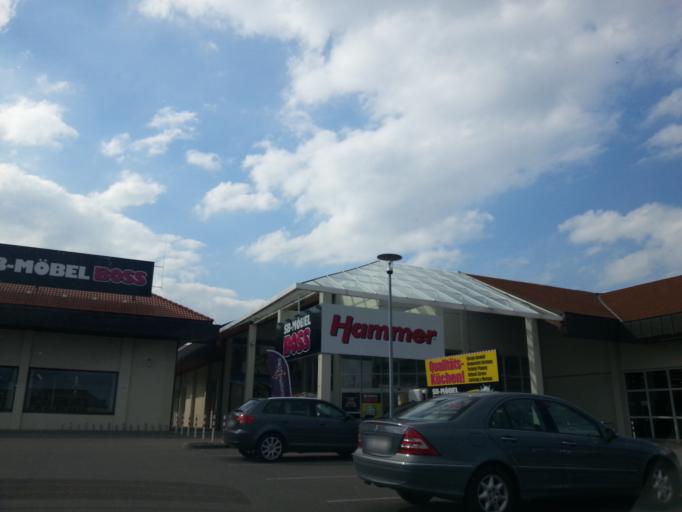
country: DE
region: Saxony
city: Freital
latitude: 51.0401
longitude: 13.6308
